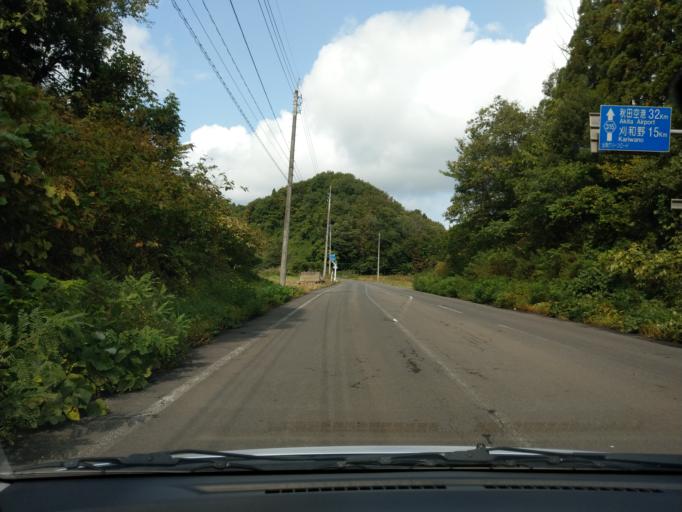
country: JP
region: Akita
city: Omagari
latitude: 39.4408
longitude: 140.3344
